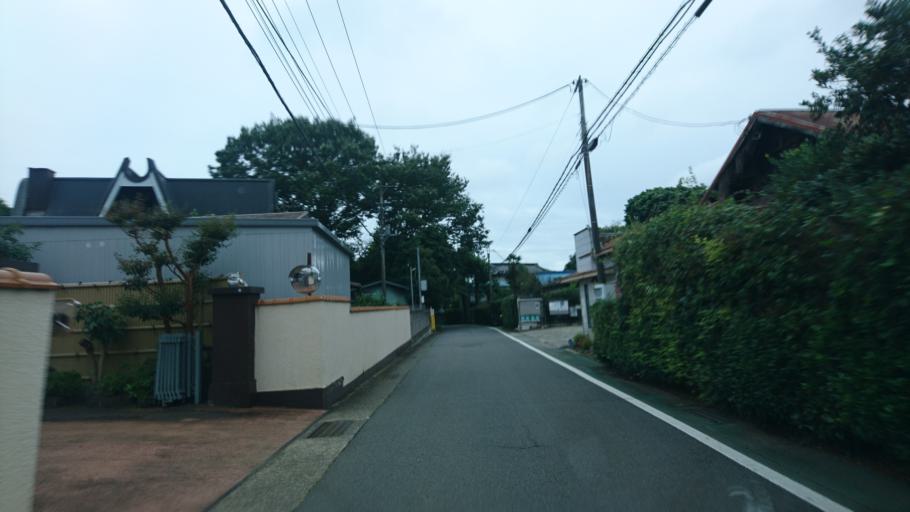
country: JP
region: Kanagawa
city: Atsugi
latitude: 35.4883
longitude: 139.3229
